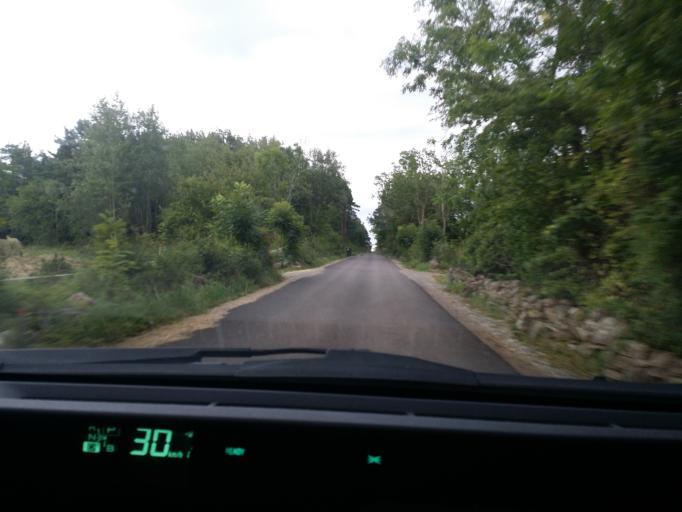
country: SE
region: Kalmar
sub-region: Borgholms Kommun
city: Borgholm
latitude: 57.2041
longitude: 16.9638
